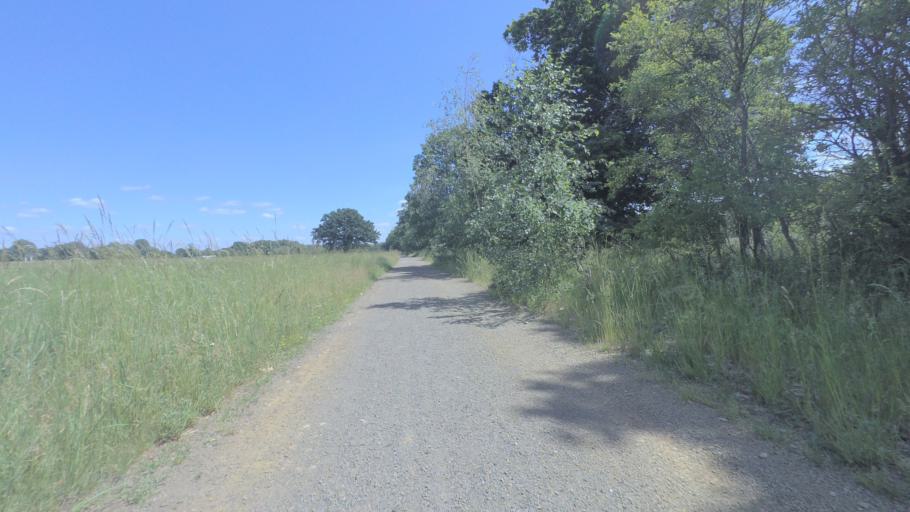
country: DE
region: Brandenburg
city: Rangsdorf
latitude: 52.3039
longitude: 13.4454
